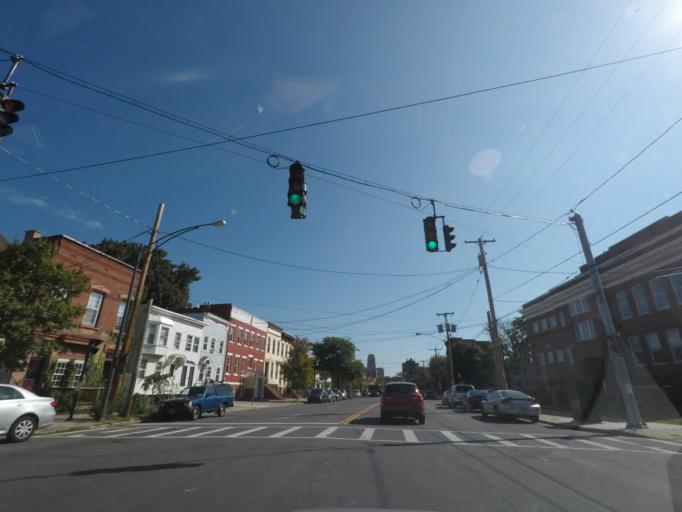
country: US
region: New York
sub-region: Albany County
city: Albany
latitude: 42.6604
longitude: -73.7697
